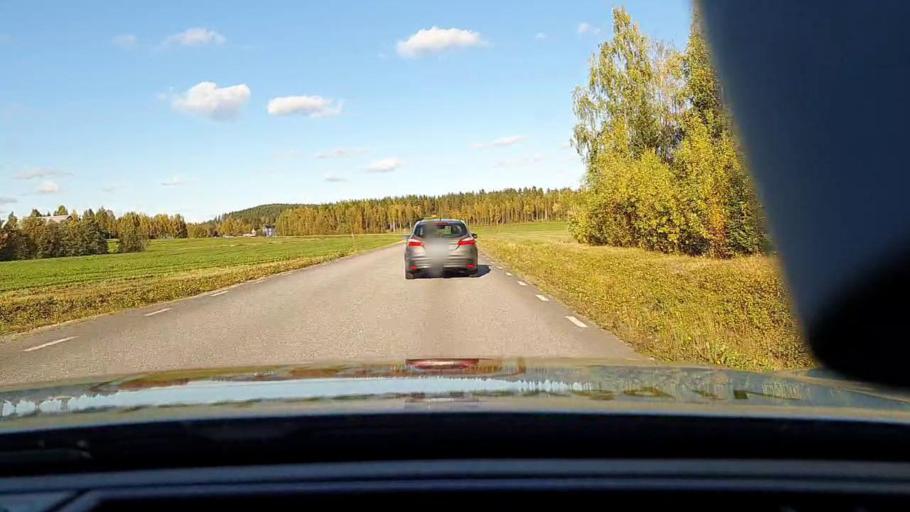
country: SE
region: Norrbotten
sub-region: Pitea Kommun
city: Norrfjarden
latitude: 65.5117
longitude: 21.4915
